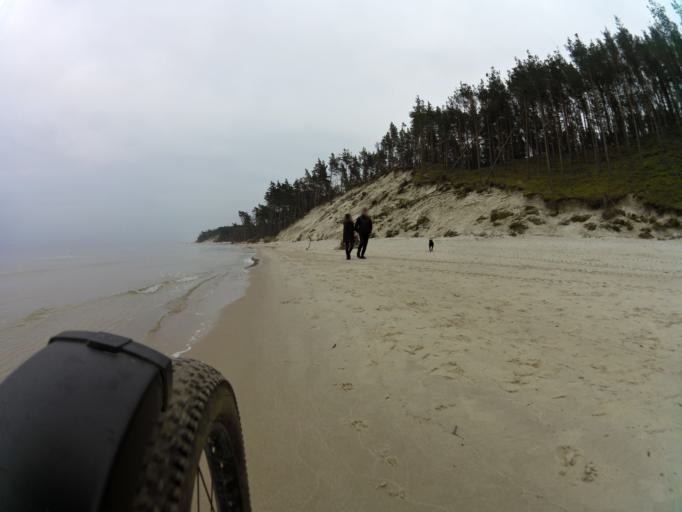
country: PL
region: Pomeranian Voivodeship
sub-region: Powiat pucki
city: Krokowa
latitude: 54.8312
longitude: 18.1344
